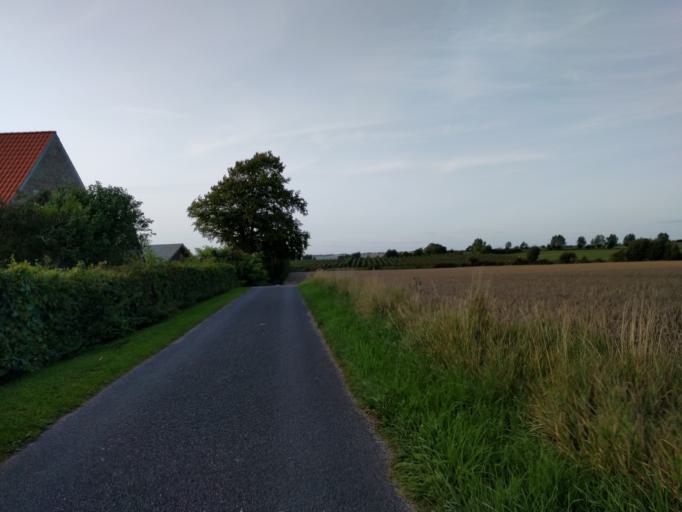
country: DK
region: South Denmark
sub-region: Kerteminde Kommune
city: Munkebo
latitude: 55.4715
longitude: 10.5799
